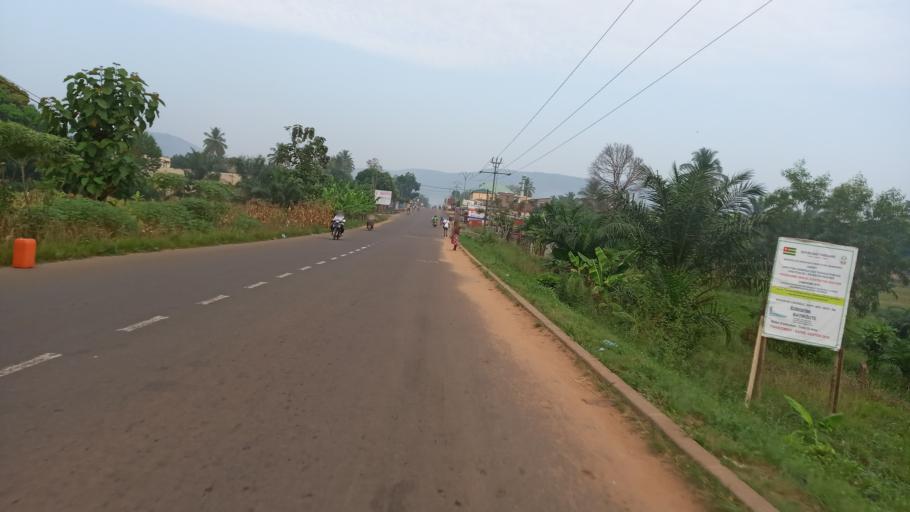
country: TG
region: Plateaux
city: Kpalime
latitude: 6.8931
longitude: 0.6399
